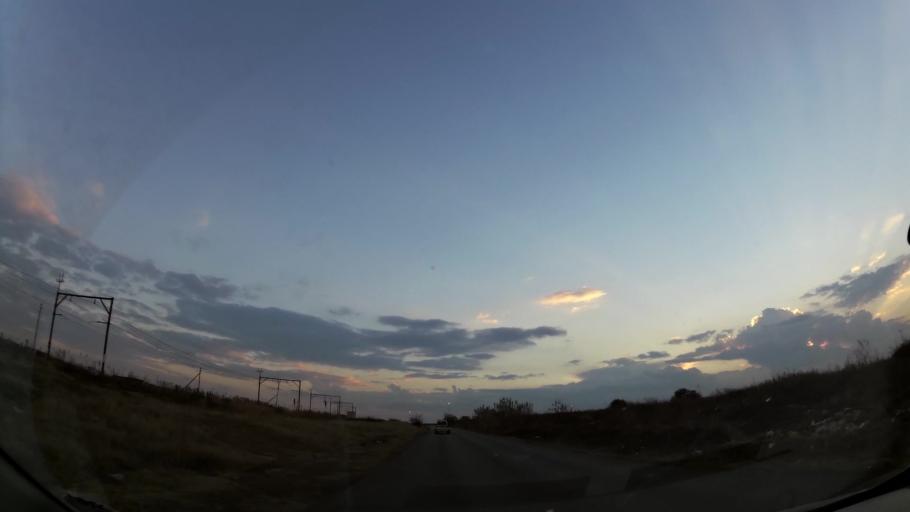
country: ZA
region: Gauteng
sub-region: City of Johannesburg Metropolitan Municipality
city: Orange Farm
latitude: -26.5641
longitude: 27.8665
